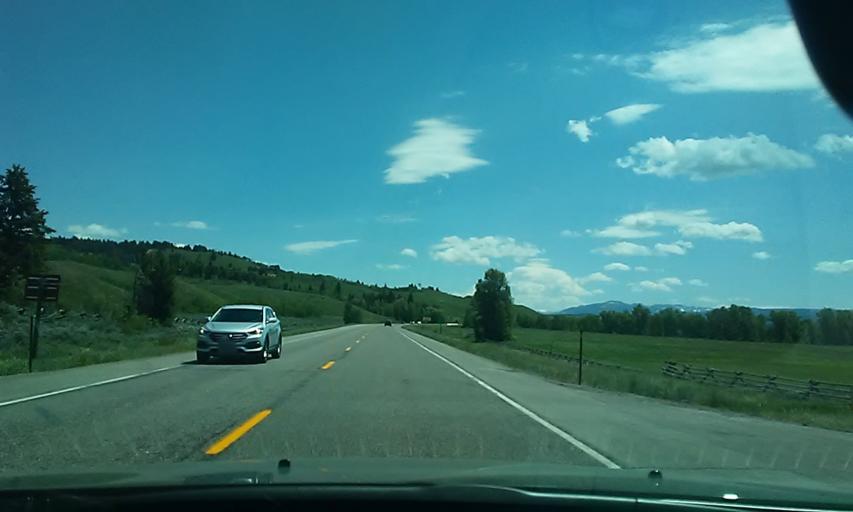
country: US
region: Wyoming
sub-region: Teton County
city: Jackson
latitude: 43.8394
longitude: -110.4659
